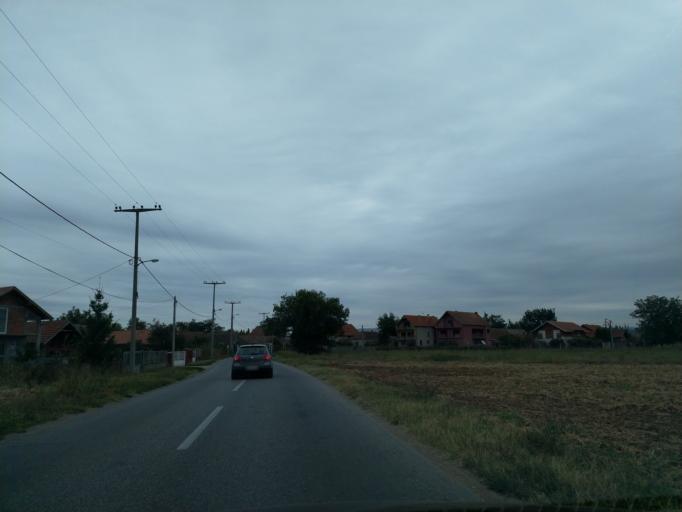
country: RS
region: Central Serbia
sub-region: Pomoravski Okrug
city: Paracin
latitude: 43.8524
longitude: 21.3920
